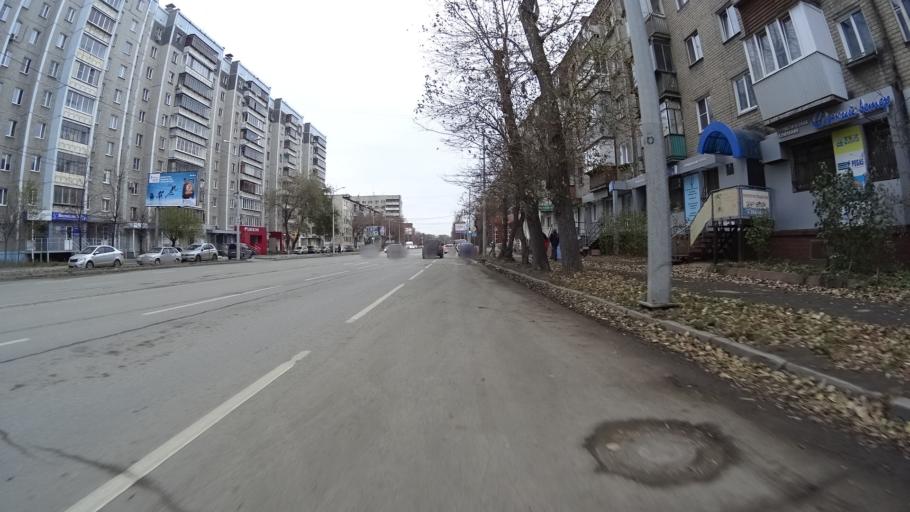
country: RU
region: Chelyabinsk
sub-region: Gorod Chelyabinsk
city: Chelyabinsk
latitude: 55.1568
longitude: 61.4173
